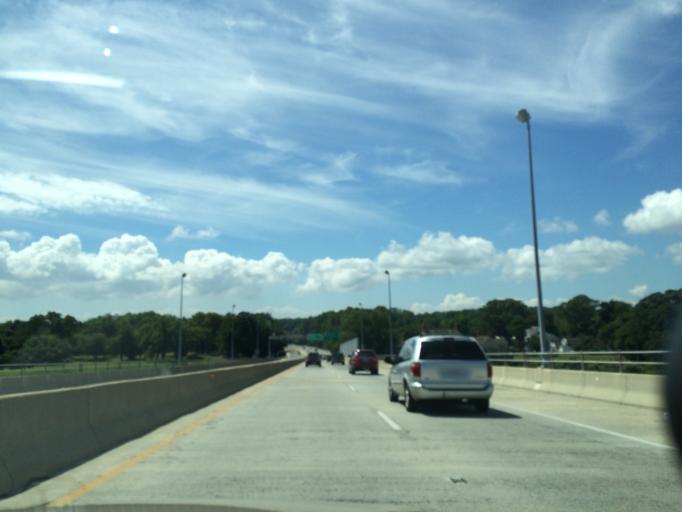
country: US
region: Virginia
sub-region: York County
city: Yorktown
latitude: 37.2402
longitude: -76.5088
